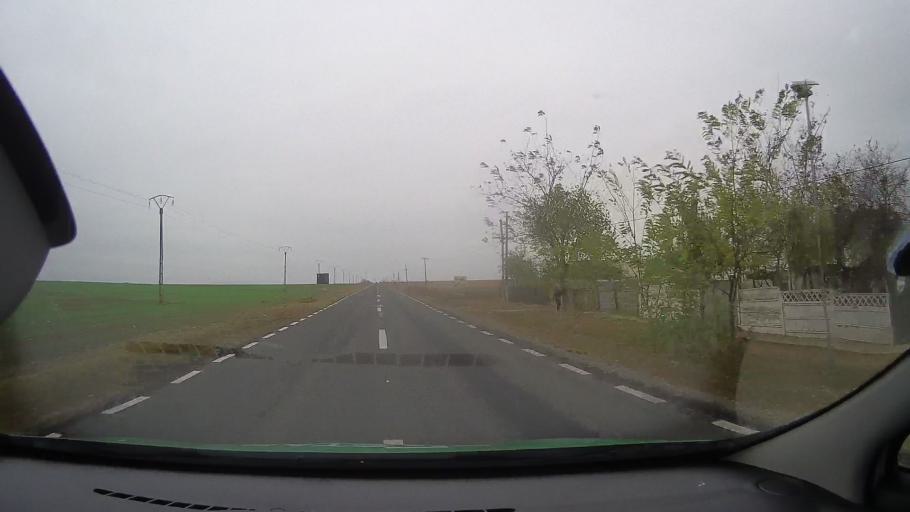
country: RO
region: Constanta
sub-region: Comuna Tortoman
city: Tortoman
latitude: 44.3508
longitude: 28.2167
